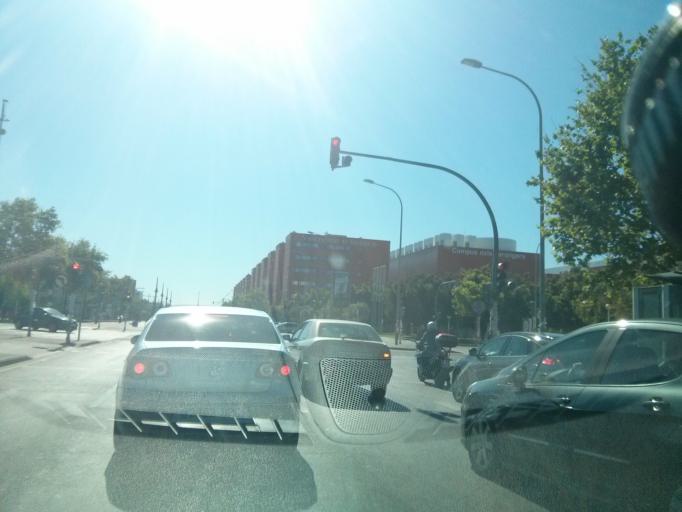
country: ES
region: Valencia
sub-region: Provincia de Valencia
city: Alboraya
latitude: 39.4799
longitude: -0.3458
